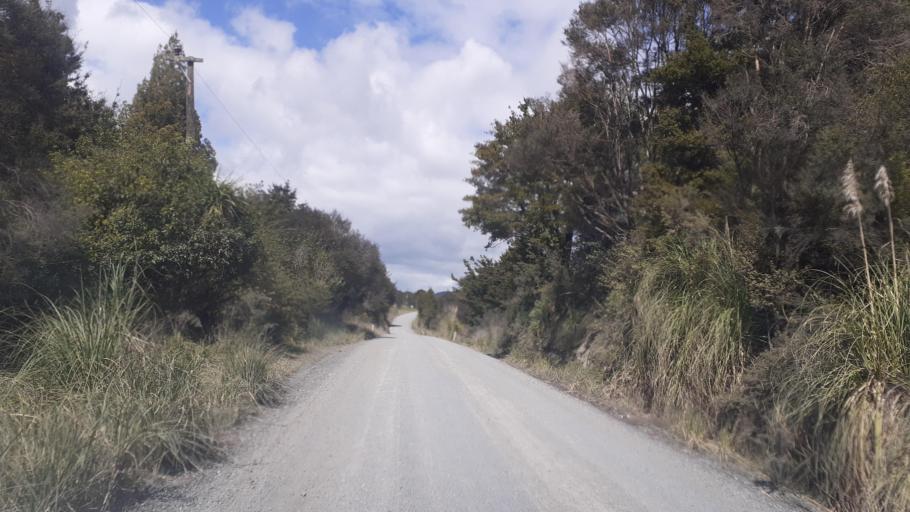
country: NZ
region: Northland
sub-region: Far North District
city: Moerewa
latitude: -35.5637
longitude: 173.9612
